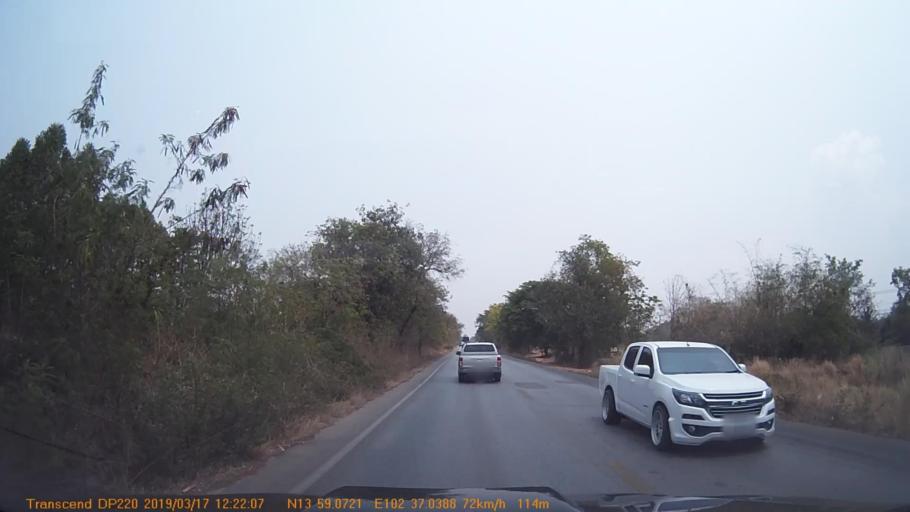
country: TH
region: Sa Kaeo
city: Khok Sung
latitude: 13.9845
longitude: 102.6176
